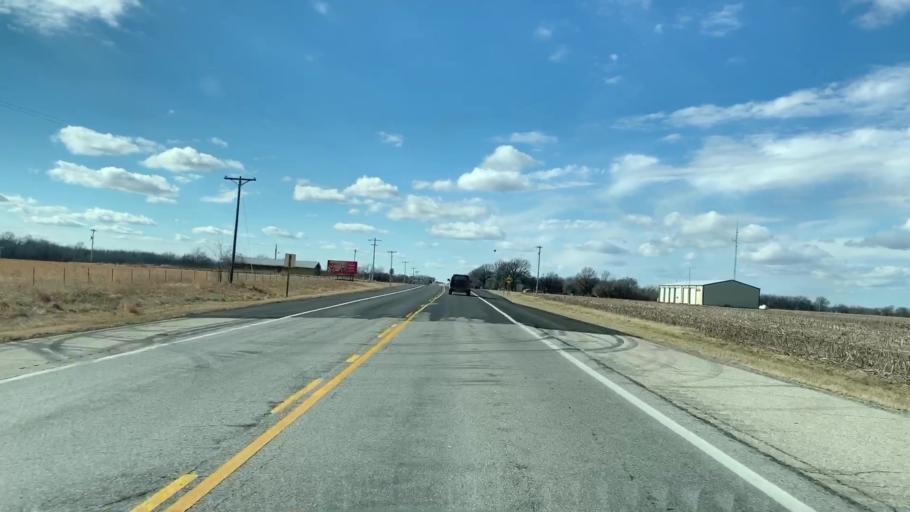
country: US
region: Kansas
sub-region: Labette County
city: Parsons
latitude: 37.3404
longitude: -95.1242
